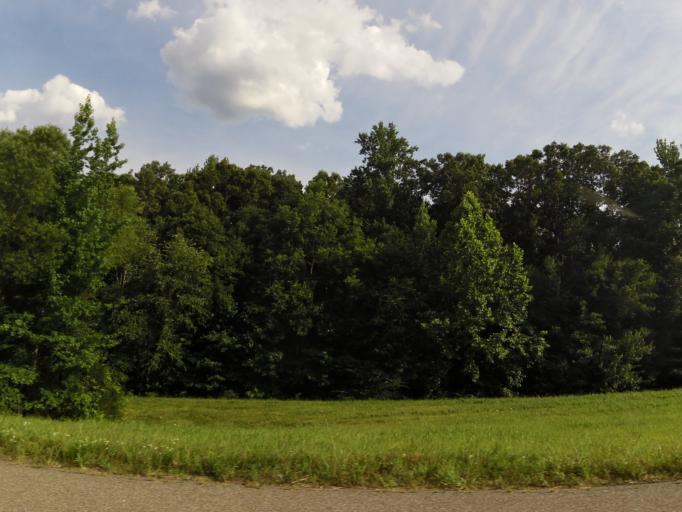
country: US
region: Tennessee
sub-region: Benton County
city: Camden
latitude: 36.0266
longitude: -88.0798
